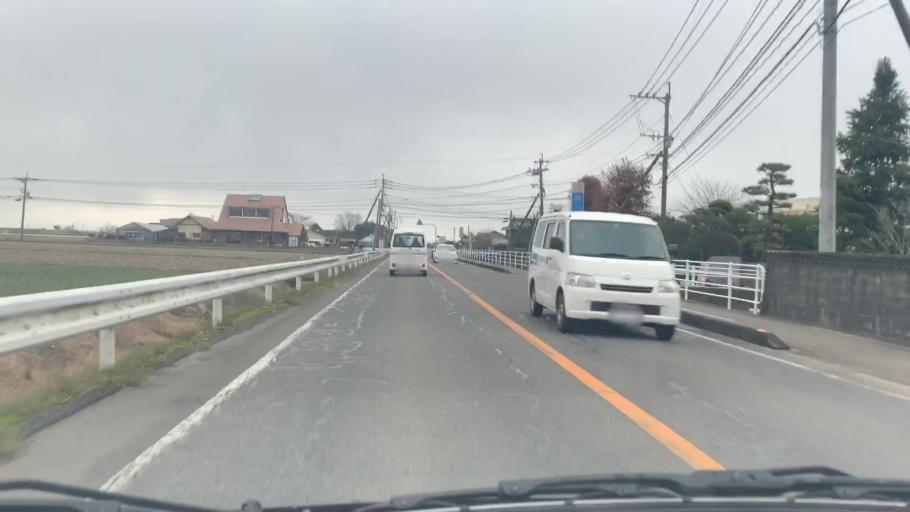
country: JP
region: Saga Prefecture
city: Kashima
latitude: 33.1857
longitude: 130.1497
